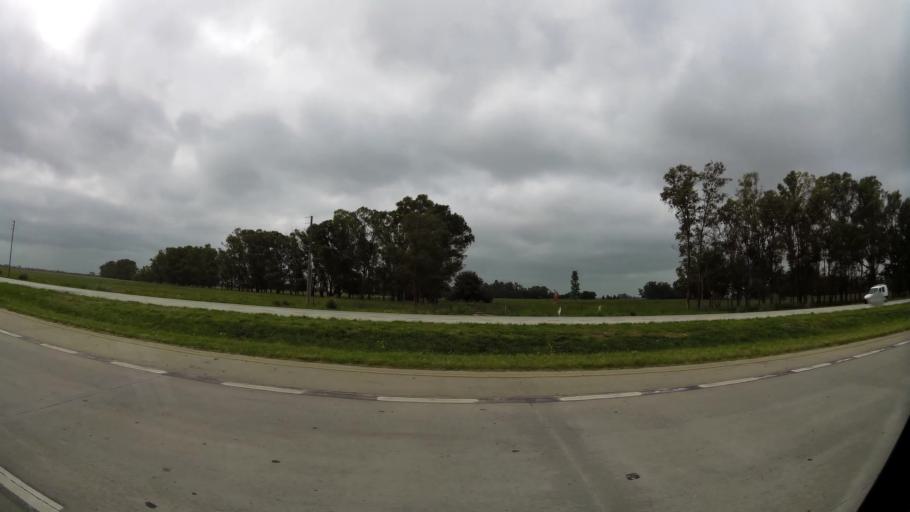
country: AR
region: Buenos Aires
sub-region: Partido de San Vicente
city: San Vicente
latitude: -35.0177
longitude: -58.2885
